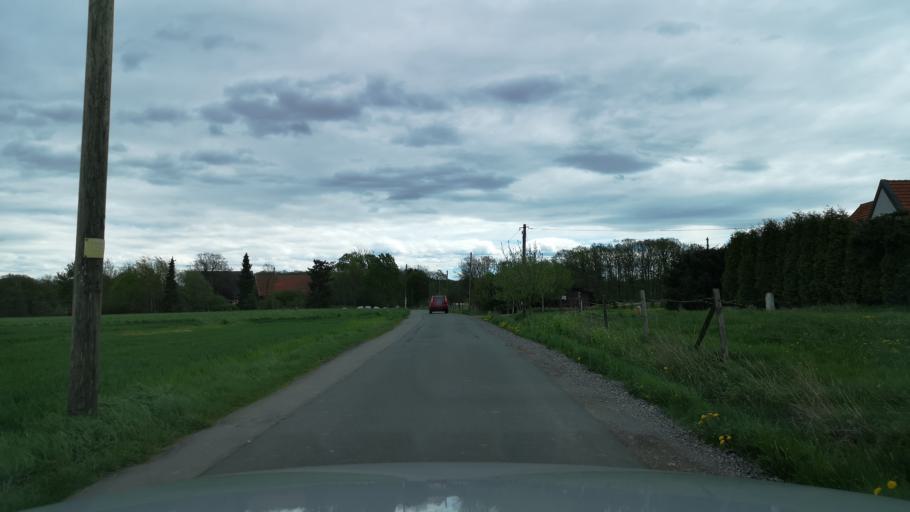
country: DE
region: North Rhine-Westphalia
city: Iserlohn
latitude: 51.4384
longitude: 7.7109
